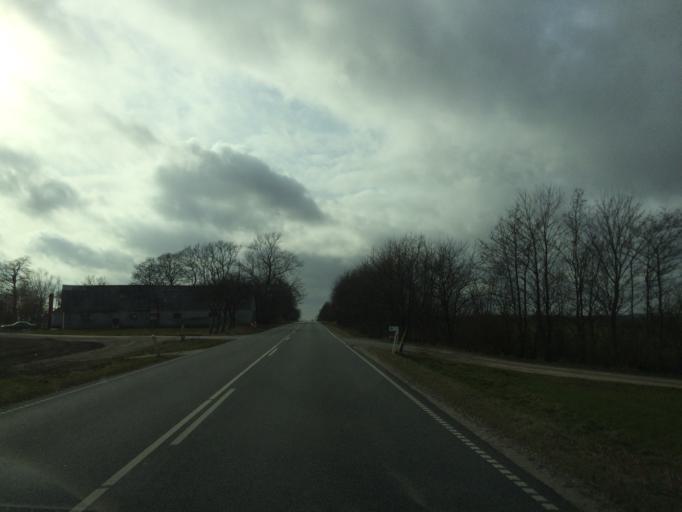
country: DK
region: Central Jutland
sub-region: Favrskov Kommune
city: Ulstrup
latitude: 56.4955
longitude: 9.8194
